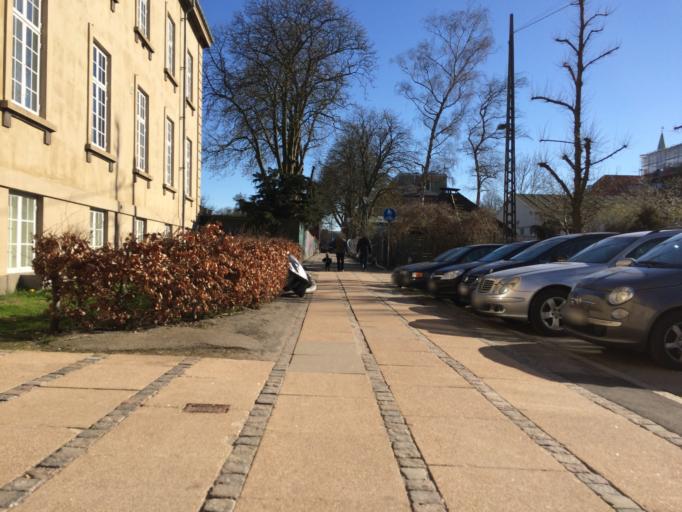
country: DK
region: Capital Region
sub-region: Kobenhavn
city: Copenhagen
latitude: 55.7130
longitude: 12.5795
